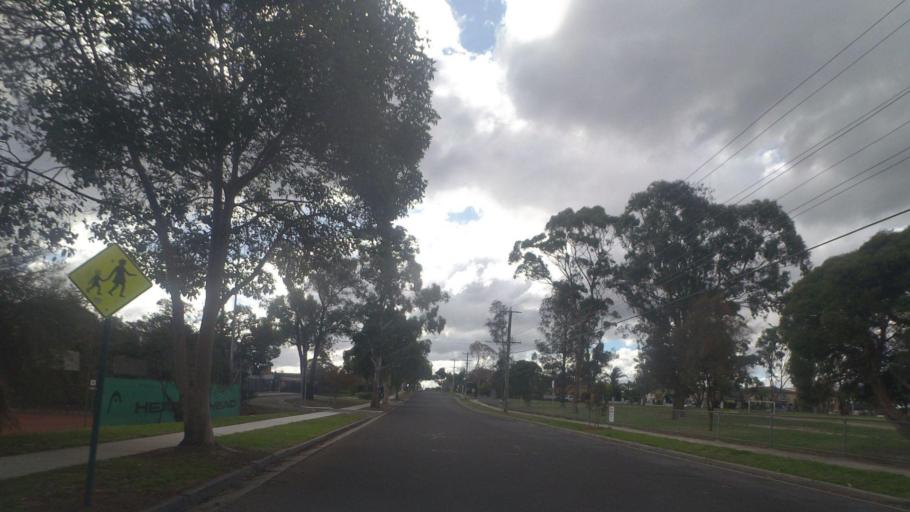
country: AU
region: Victoria
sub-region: Whitehorse
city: Vermont South
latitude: -37.8519
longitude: 145.1806
